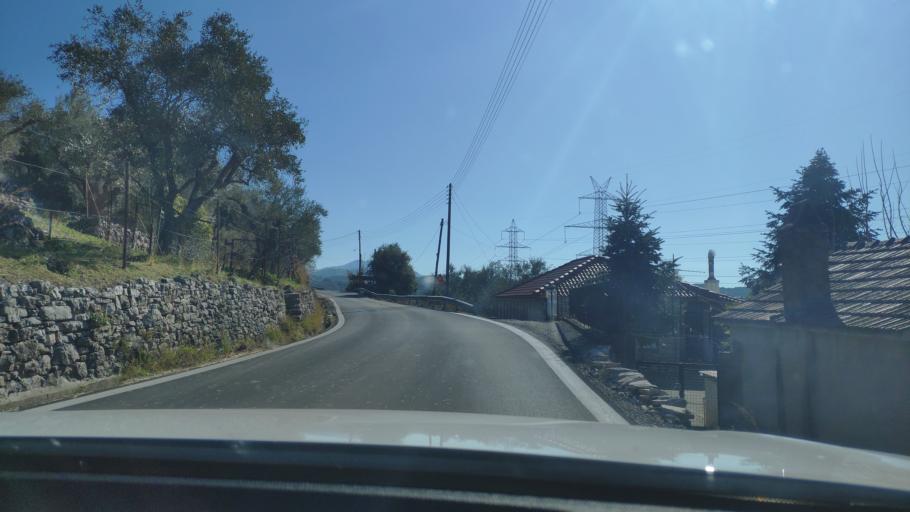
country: GR
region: West Greece
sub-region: Nomos Aitolias kai Akarnanias
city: Thermo
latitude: 38.5844
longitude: 21.6307
